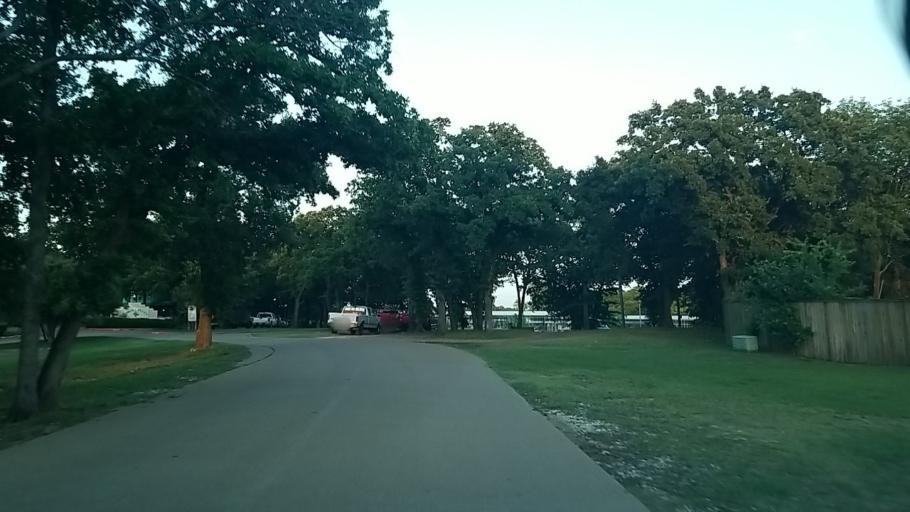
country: US
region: Texas
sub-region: Denton County
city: Highland Village
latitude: 33.0835
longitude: -97.0208
